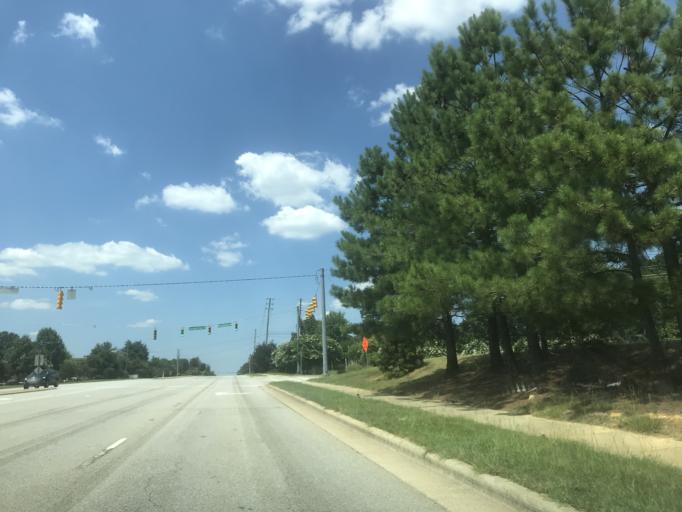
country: US
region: North Carolina
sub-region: Wake County
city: Cary
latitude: 35.7497
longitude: -78.7409
